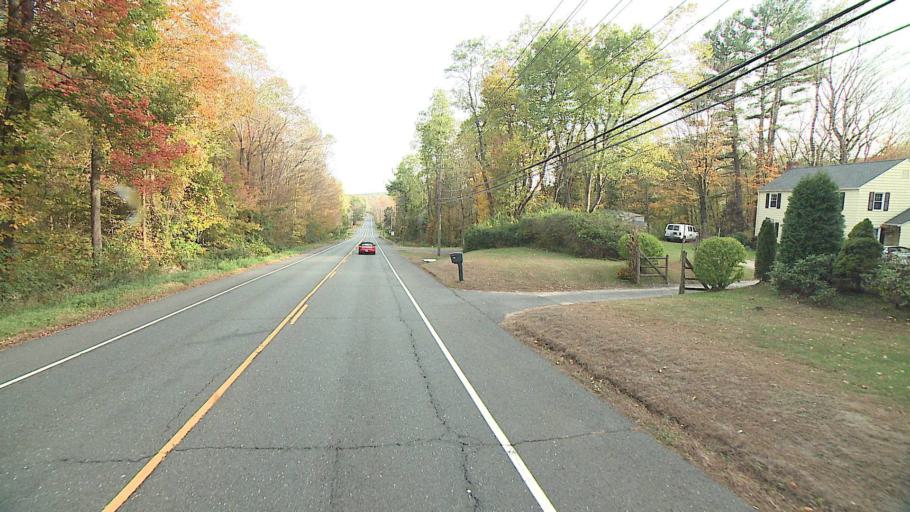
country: US
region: Connecticut
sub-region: Hartford County
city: Collinsville
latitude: 41.8469
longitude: -72.9446
